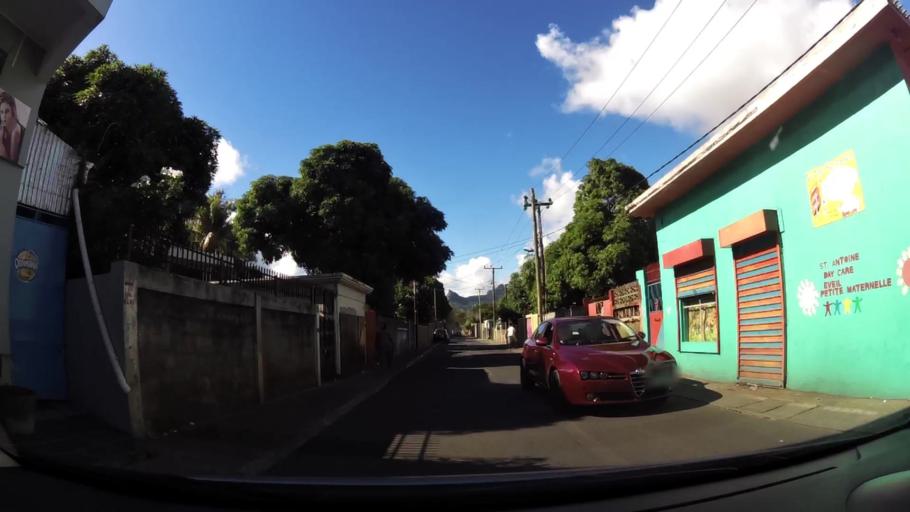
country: MU
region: Pamplemousses
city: Le Hochet
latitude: -20.1461
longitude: 57.5168
